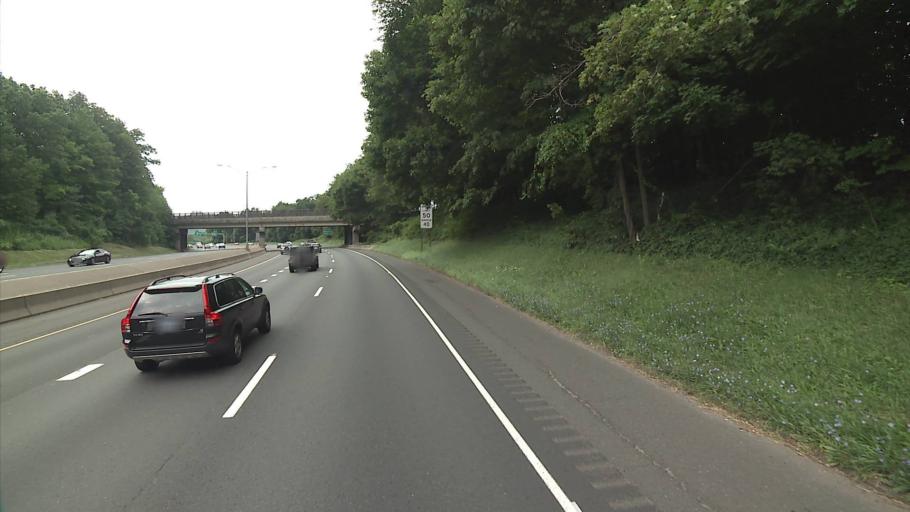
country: US
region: Connecticut
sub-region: Fairfield County
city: Danbury
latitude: 41.3953
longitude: -73.4781
